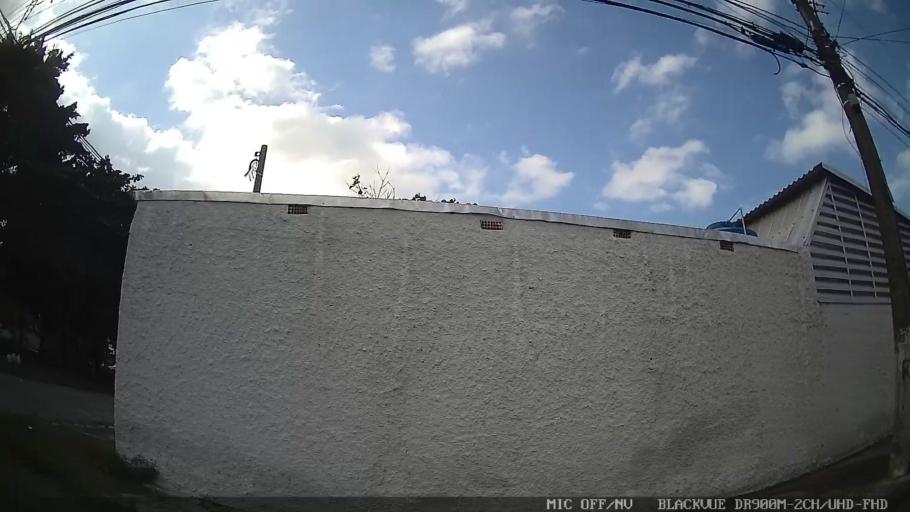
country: BR
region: Sao Paulo
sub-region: Guaruja
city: Guaruja
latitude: -23.9929
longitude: -46.2792
